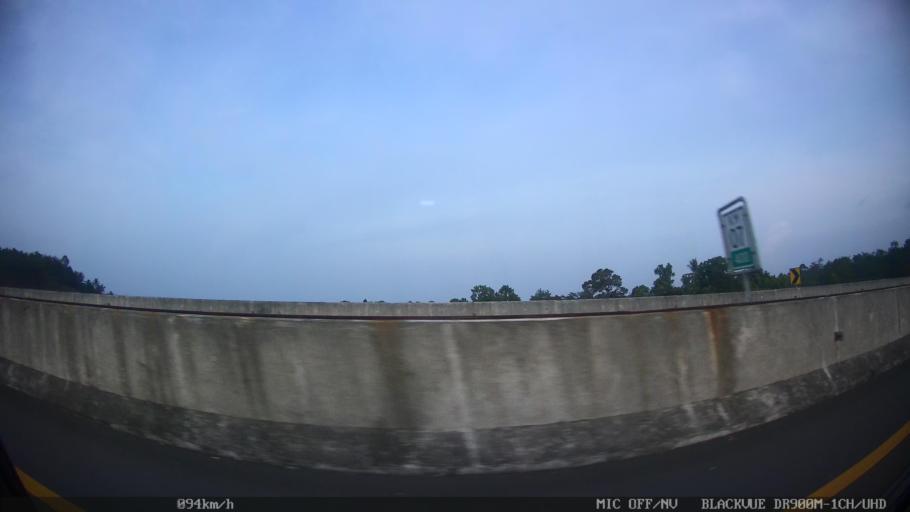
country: ID
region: Lampung
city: Penengahan
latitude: -5.8174
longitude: 105.7369
